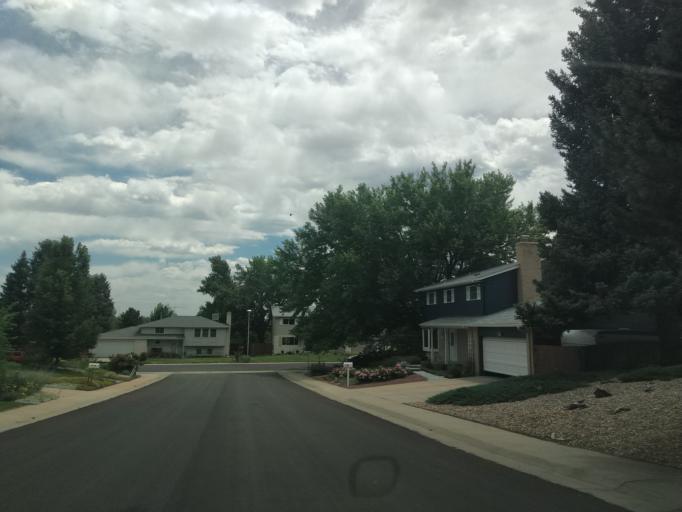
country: US
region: Colorado
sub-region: Jefferson County
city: Lakewood
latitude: 39.6723
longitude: -105.1014
